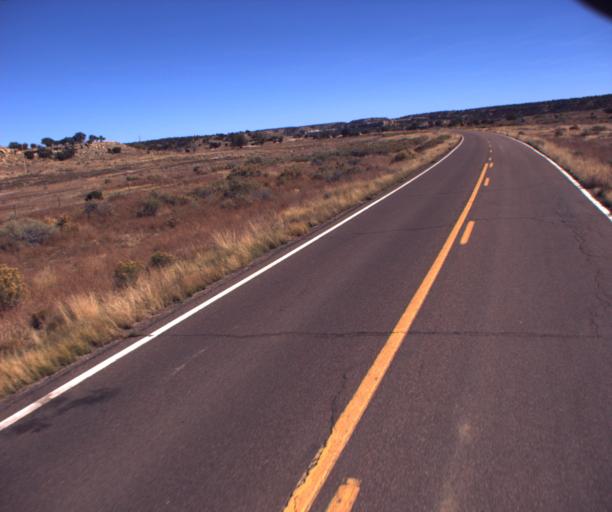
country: US
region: Arizona
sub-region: Apache County
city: Ganado
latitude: 35.7470
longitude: -109.8690
